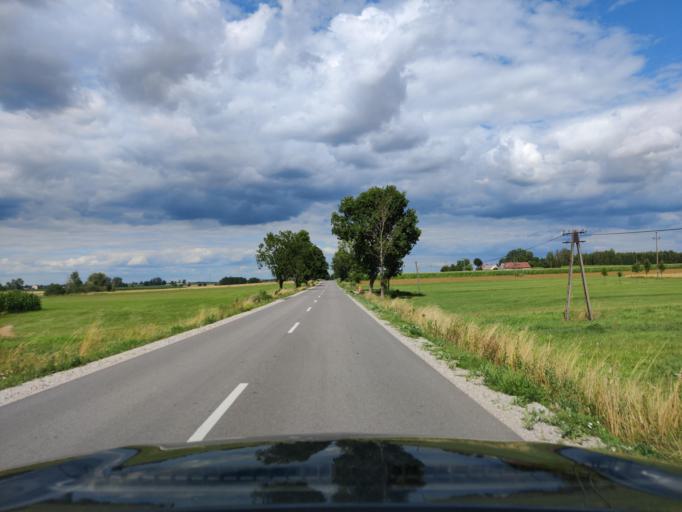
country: PL
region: Masovian Voivodeship
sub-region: Powiat sokolowski
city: Kosow Lacki
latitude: 52.5641
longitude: 22.1191
